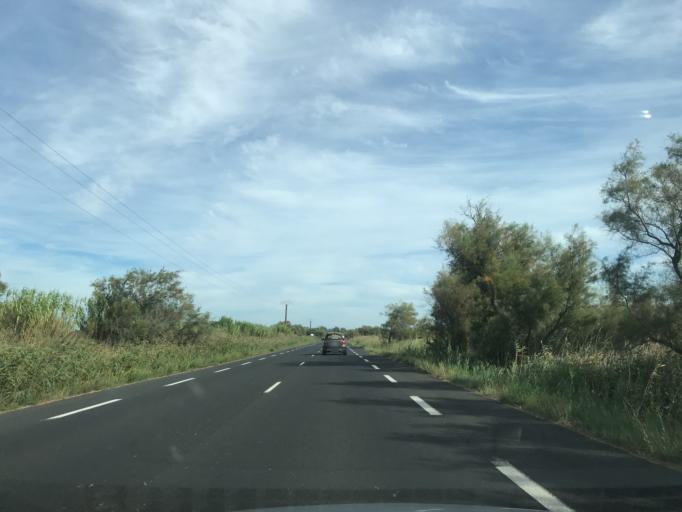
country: FR
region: Provence-Alpes-Cote d'Azur
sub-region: Departement des Bouches-du-Rhone
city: Saintes-Maries-de-la-Mer
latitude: 43.5510
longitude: 4.3367
